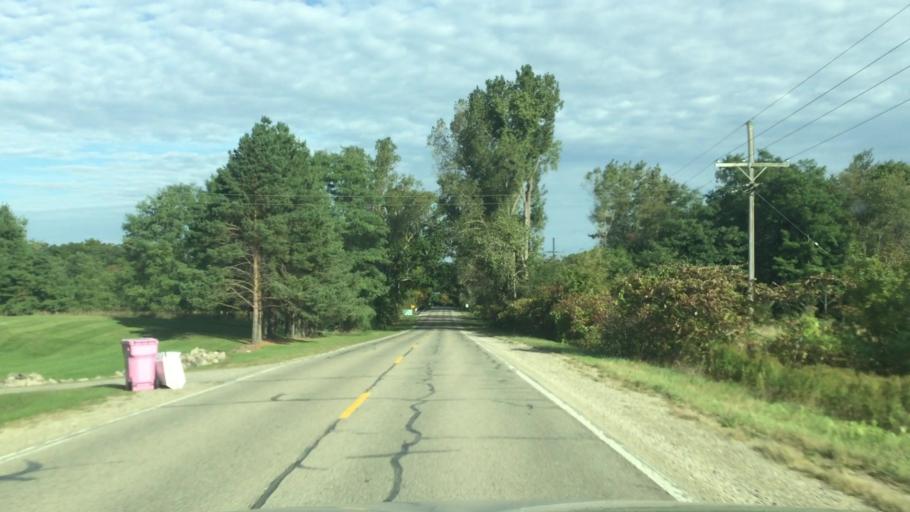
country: US
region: Michigan
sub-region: Livingston County
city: Howell
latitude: 42.5586
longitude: -83.8878
